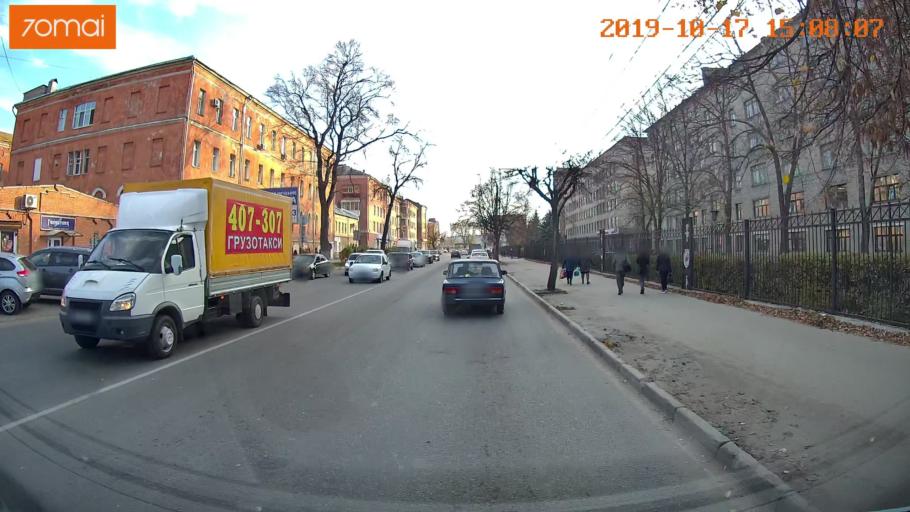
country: RU
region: Rjazan
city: Ryazan'
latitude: 54.6316
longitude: 39.7241
